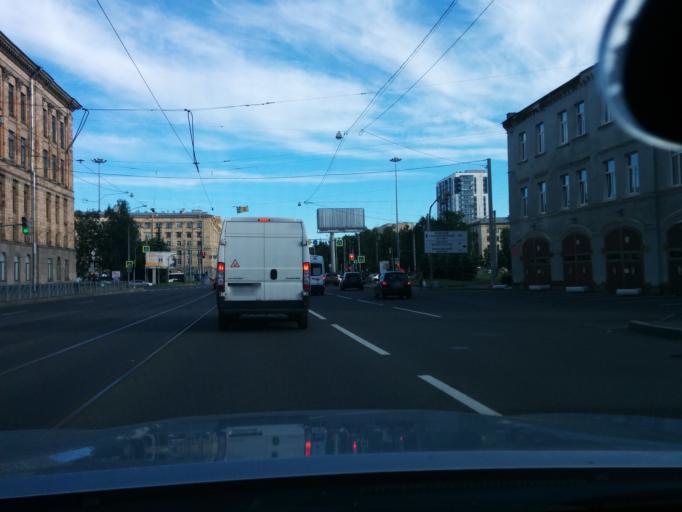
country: RU
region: Leningrad
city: Svetlanovskiy
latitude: 60.0048
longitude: 30.3271
